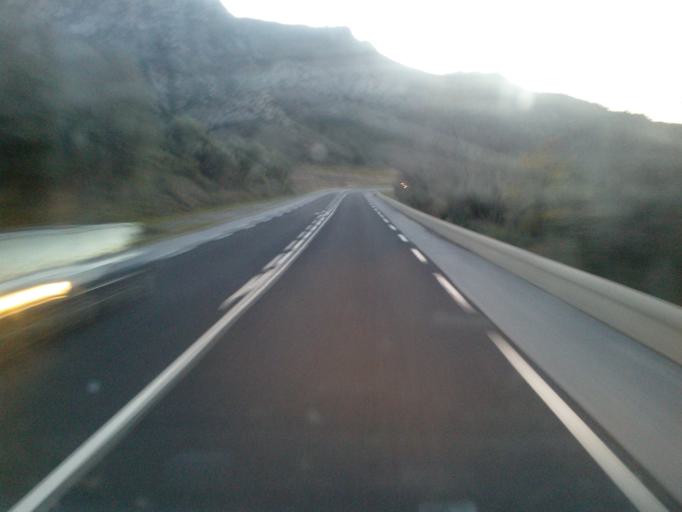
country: FR
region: Languedoc-Roussillon
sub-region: Departement des Pyrenees-Orientales
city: Baixas
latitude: 42.7749
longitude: 2.7668
